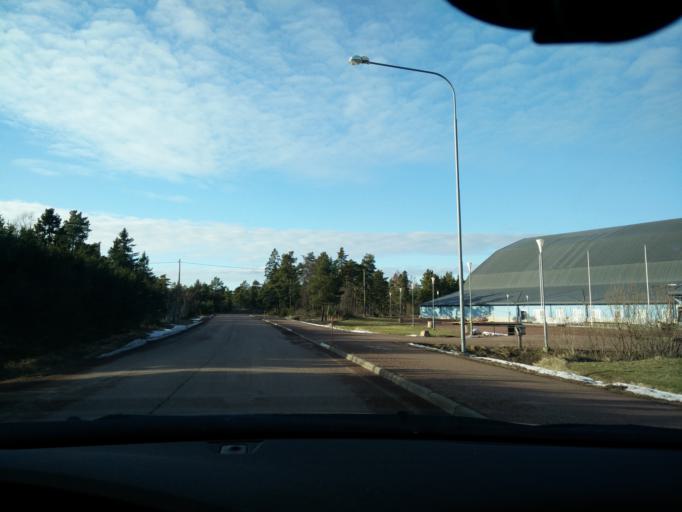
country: AX
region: Alands landsbygd
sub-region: Eckeroe
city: Eckeroe
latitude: 60.2285
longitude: 19.5493
